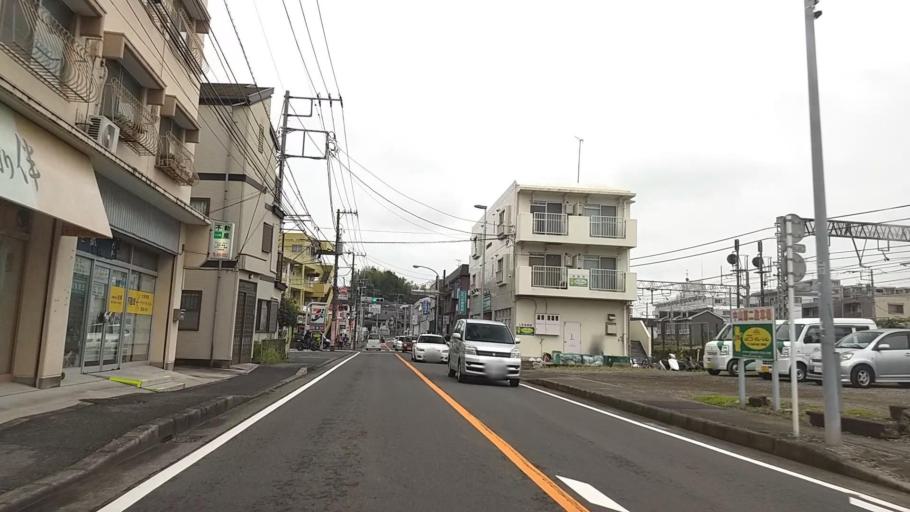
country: JP
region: Kanagawa
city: Fujisawa
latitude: 35.3957
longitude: 139.5361
